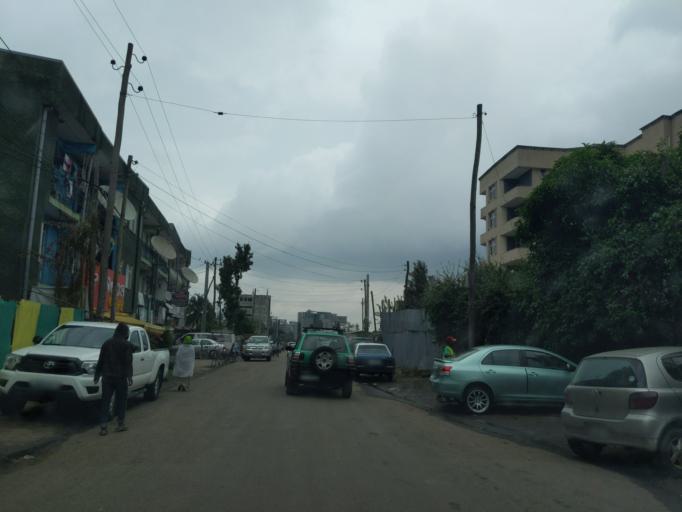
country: ET
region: Adis Abeba
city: Addis Ababa
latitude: 8.9981
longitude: 38.7689
